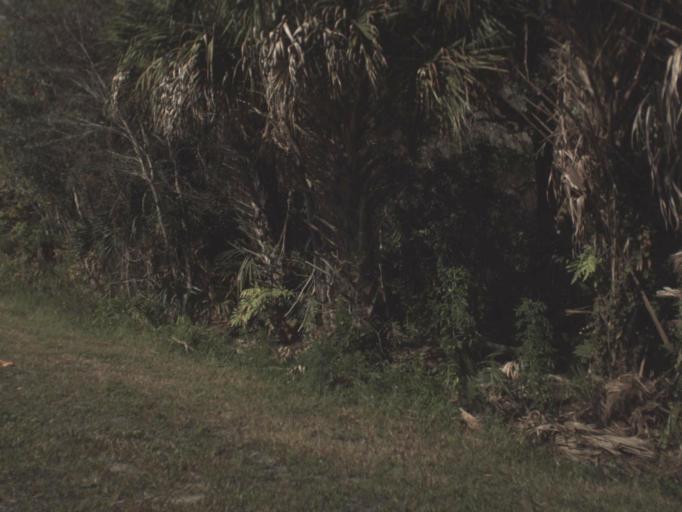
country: US
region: Florida
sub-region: Brevard County
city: Merritt Island
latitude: 28.6437
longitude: -80.6863
